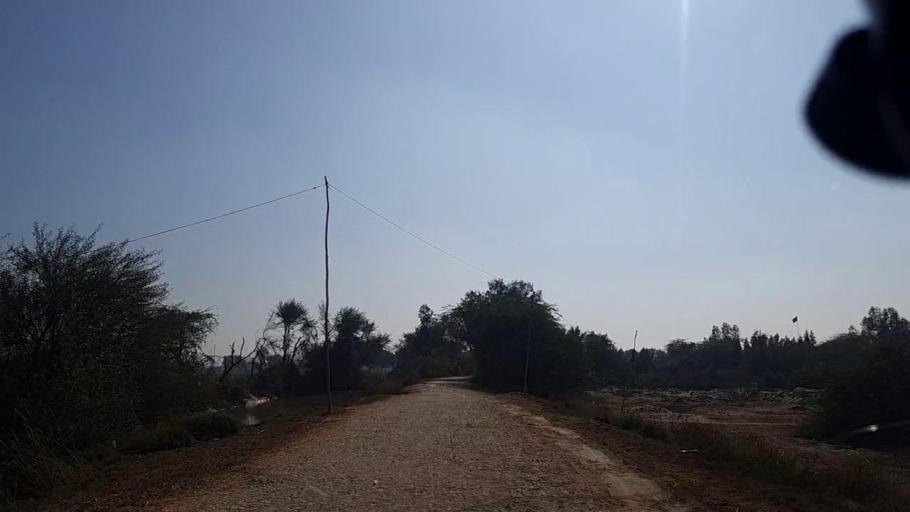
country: PK
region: Sindh
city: Khanpur
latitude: 27.7758
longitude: 69.4228
